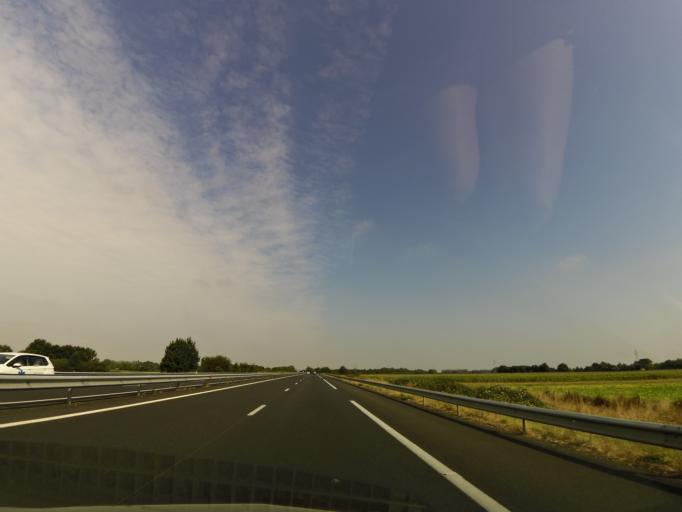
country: FR
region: Pays de la Loire
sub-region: Departement de la Vendee
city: Les Brouzils
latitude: 46.8882
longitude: -1.2941
